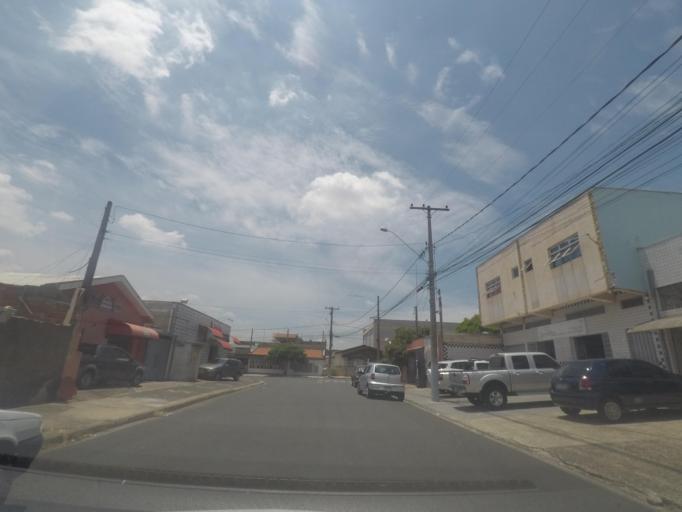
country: BR
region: Sao Paulo
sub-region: Nova Odessa
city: Nova Odessa
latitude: -22.7972
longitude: -47.2791
